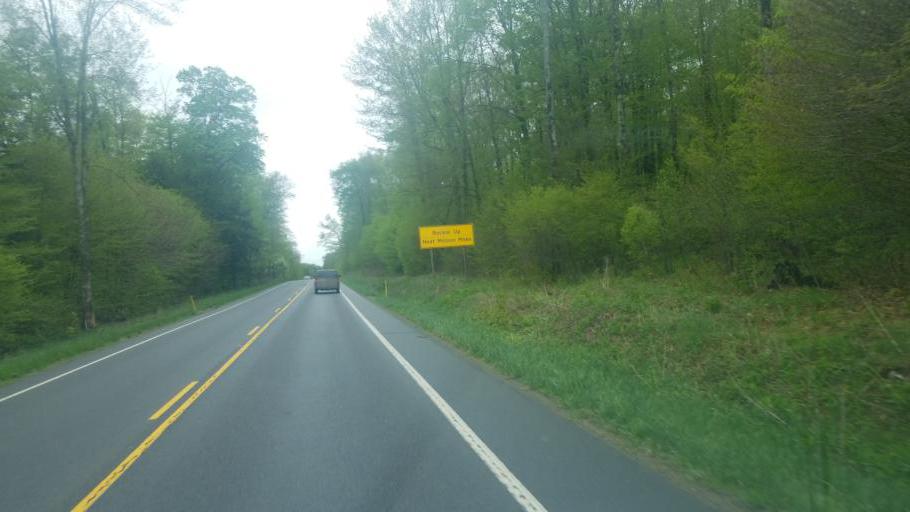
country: US
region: Pennsylvania
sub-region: McKean County
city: Kane
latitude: 41.5773
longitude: -78.9246
